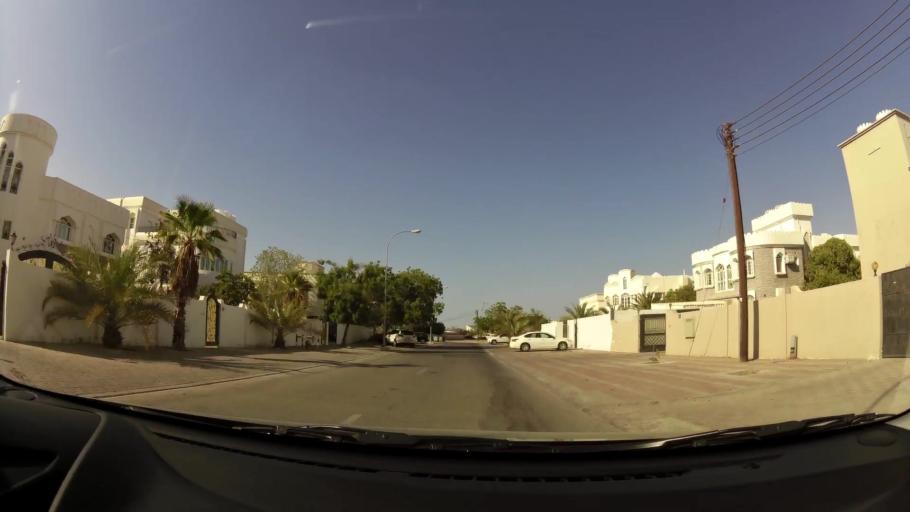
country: OM
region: Muhafazat Masqat
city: As Sib al Jadidah
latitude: 23.6158
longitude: 58.2125
